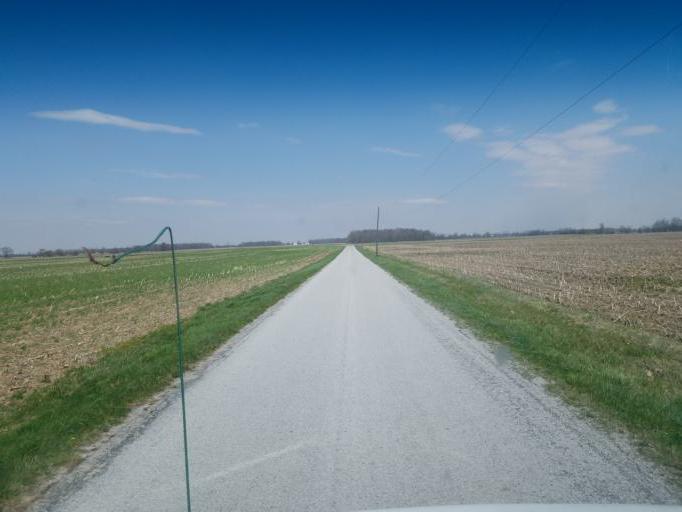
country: US
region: Ohio
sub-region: Hardin County
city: Kenton
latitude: 40.6985
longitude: -83.5473
